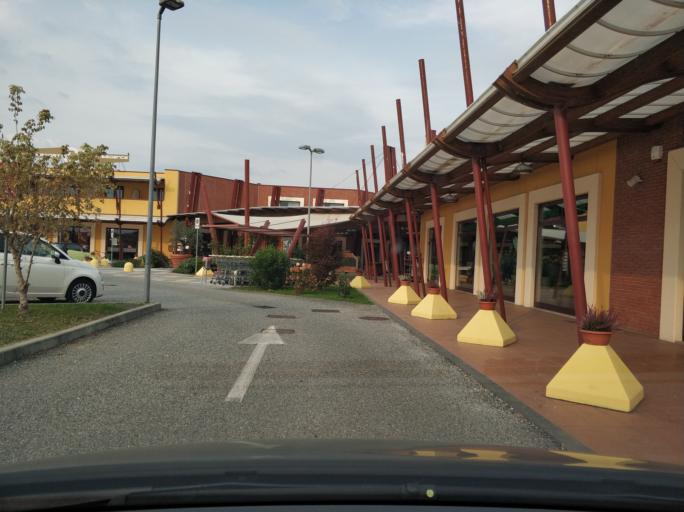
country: IT
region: Piedmont
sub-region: Provincia di Torino
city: San Francesco al Campo
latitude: 45.2340
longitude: 7.6523
